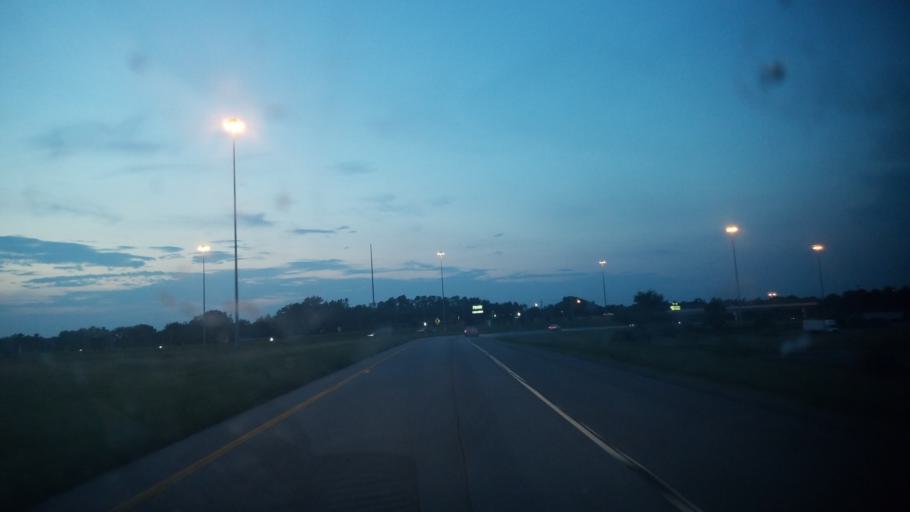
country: US
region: Ohio
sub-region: Clermont County
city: Summerside
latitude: 39.1024
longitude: -84.2815
